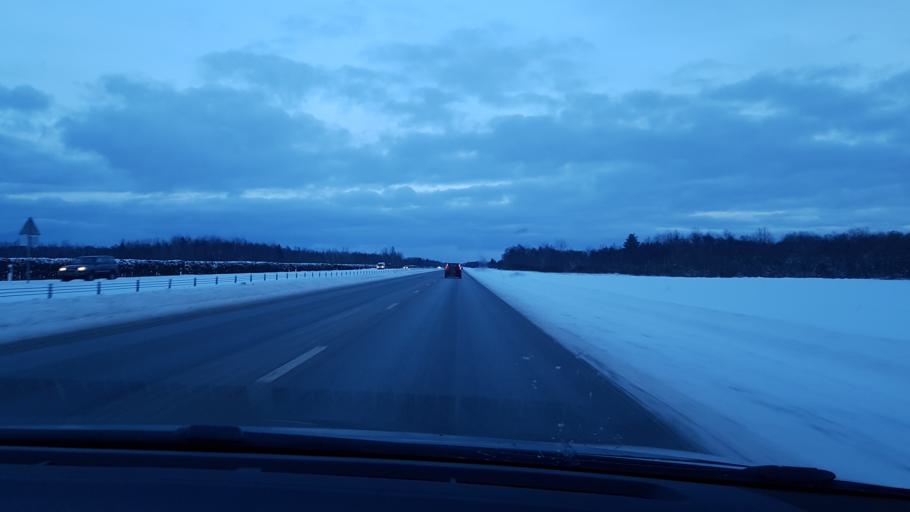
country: EE
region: Harju
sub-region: Anija vald
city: Kehra
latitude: 59.4416
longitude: 25.3127
